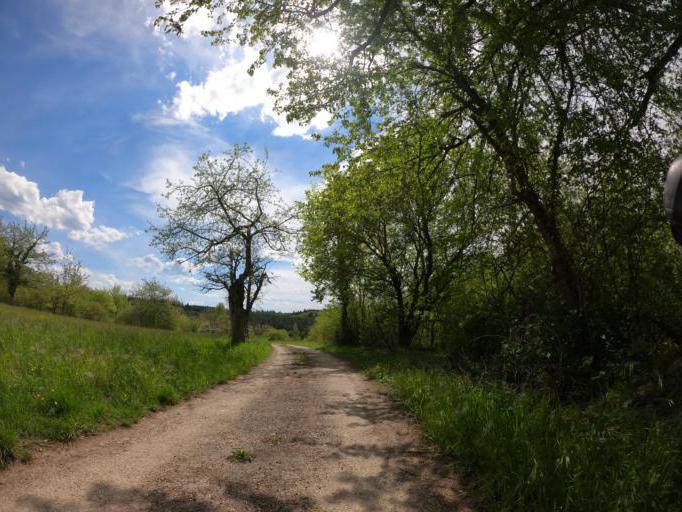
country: DE
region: Baden-Wuerttemberg
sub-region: Karlsruhe Region
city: Konigsbach-Stein
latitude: 48.9331
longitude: 8.6097
